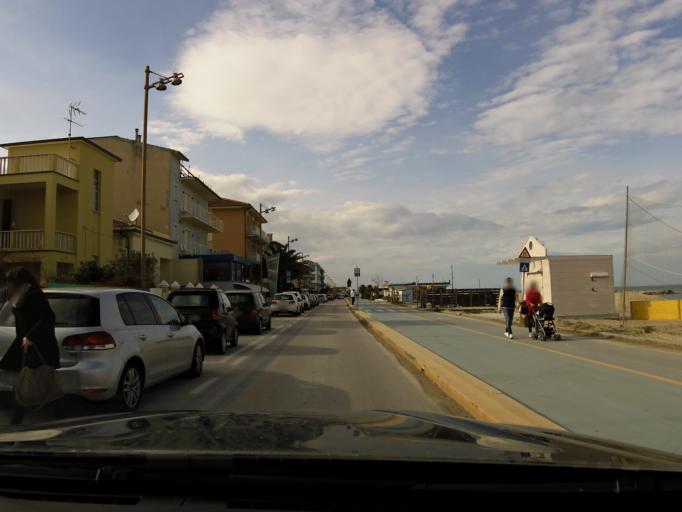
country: IT
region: The Marches
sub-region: Provincia di Macerata
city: Civitanova Marche
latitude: 43.3260
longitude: 13.7164
